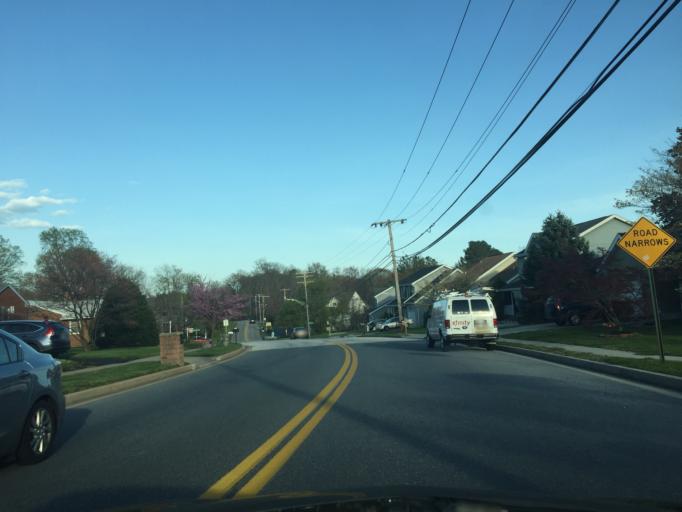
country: US
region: Maryland
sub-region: Baltimore County
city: Perry Hall
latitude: 39.3996
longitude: -76.4694
